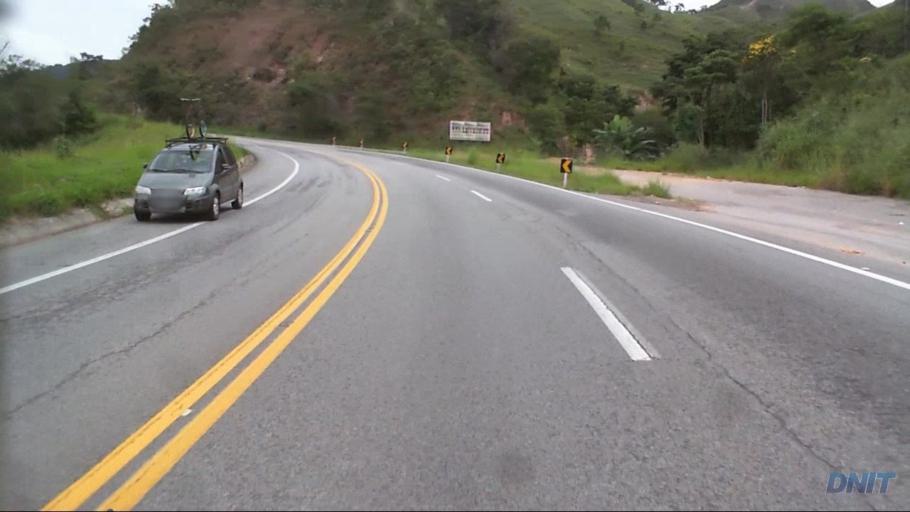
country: BR
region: Minas Gerais
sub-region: Nova Era
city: Nova Era
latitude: -19.6309
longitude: -42.8871
